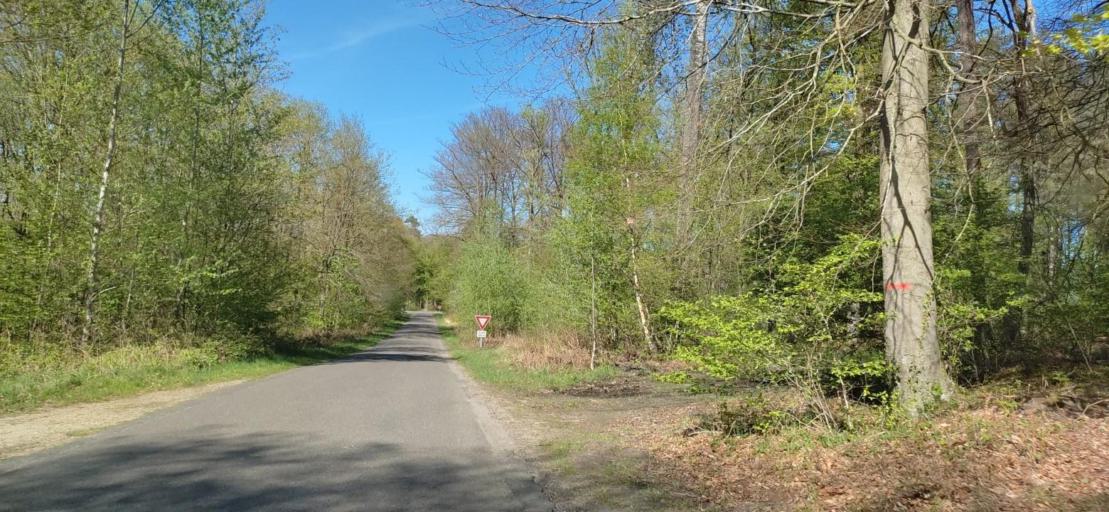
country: FR
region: Picardie
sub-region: Departement de l'Oise
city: Le Plessis-Brion
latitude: 49.4525
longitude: 2.9240
